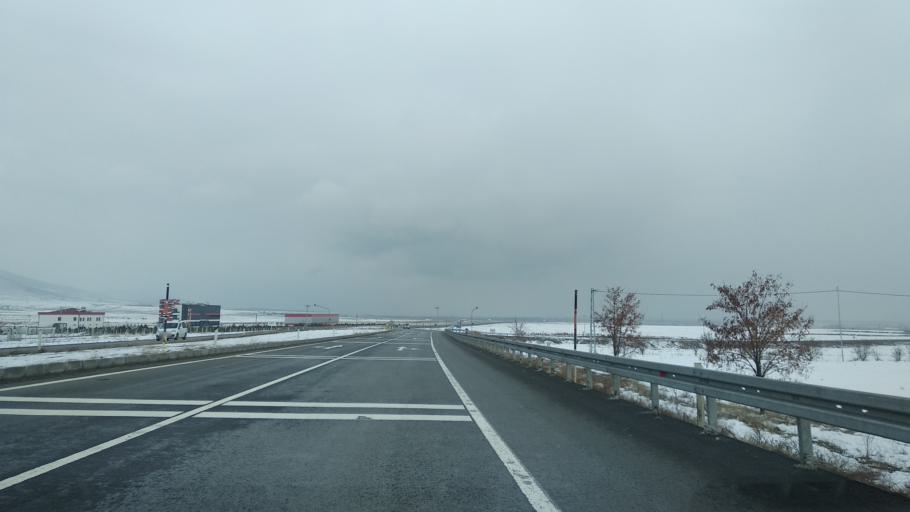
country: TR
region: Kayseri
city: Elbasi
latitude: 38.6352
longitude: 35.8517
